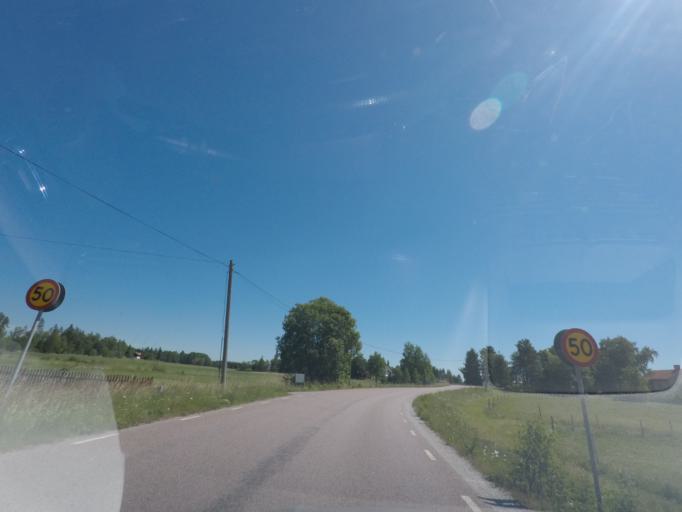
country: SE
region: Uppsala
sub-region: Enkopings Kommun
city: Irsta
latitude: 59.6816
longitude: 16.8132
